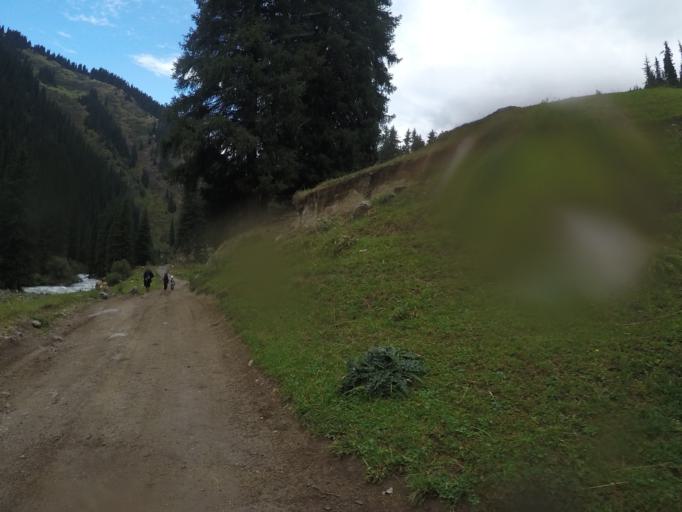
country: KG
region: Ysyk-Koel
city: Teploklyuchenka
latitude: 42.4125
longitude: 78.5749
